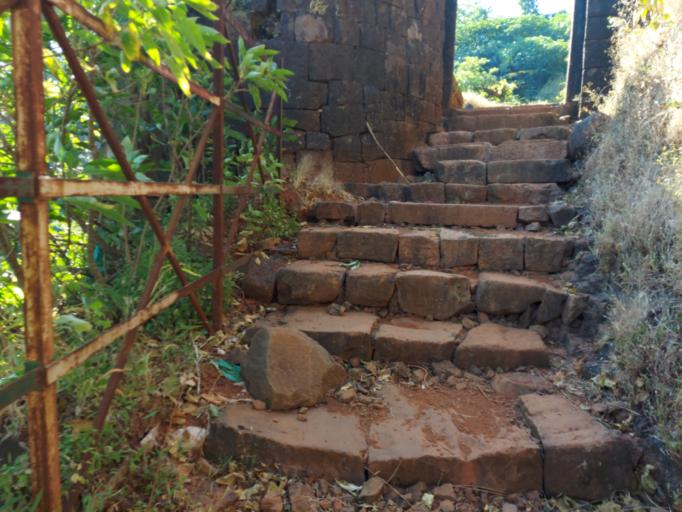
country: IN
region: Maharashtra
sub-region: Sindhudurg
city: Kudal
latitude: 16.0847
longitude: 73.8438
